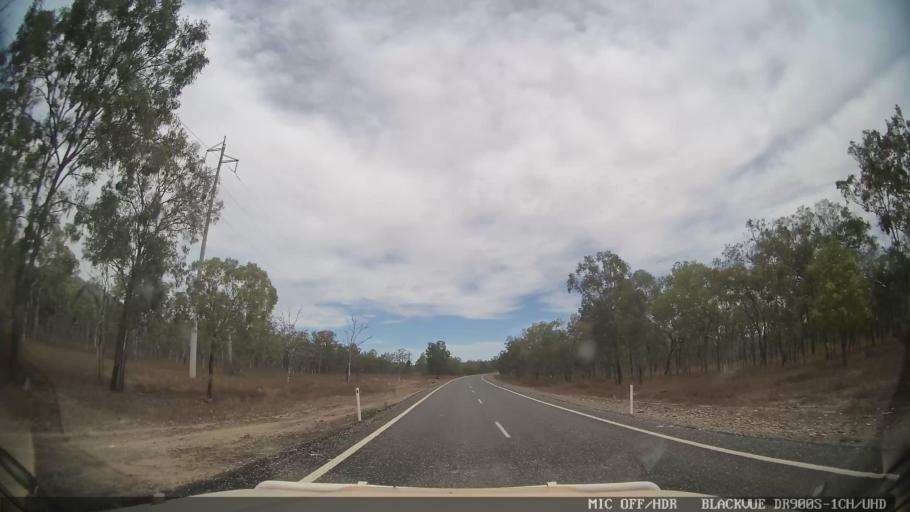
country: AU
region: Queensland
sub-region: Cairns
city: Port Douglas
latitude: -16.2511
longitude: 144.7260
